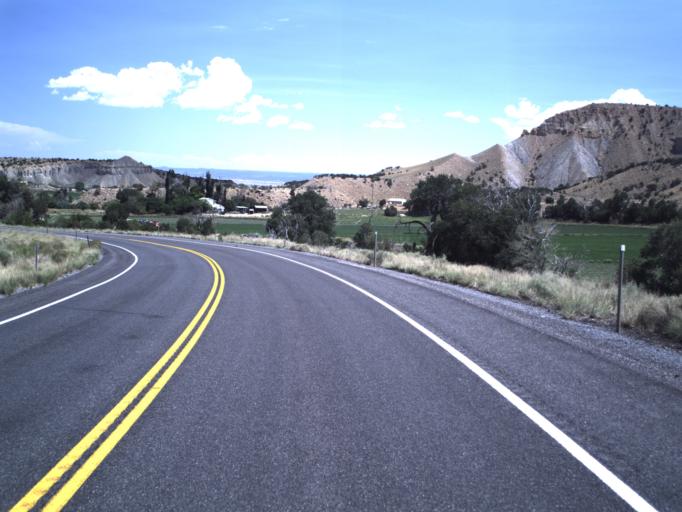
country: US
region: Utah
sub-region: Emery County
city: Huntington
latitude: 39.3625
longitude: -111.0474
